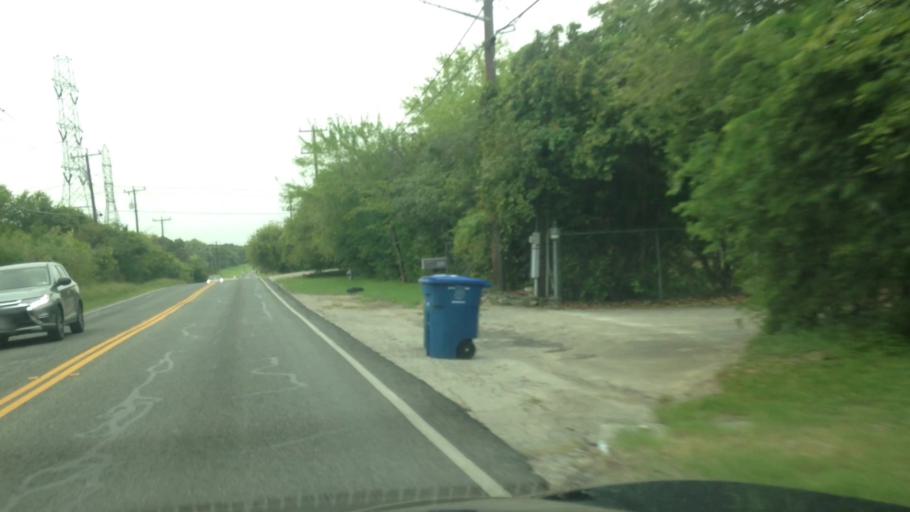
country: US
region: Texas
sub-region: Bexar County
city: Windcrest
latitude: 29.5767
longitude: -98.4029
